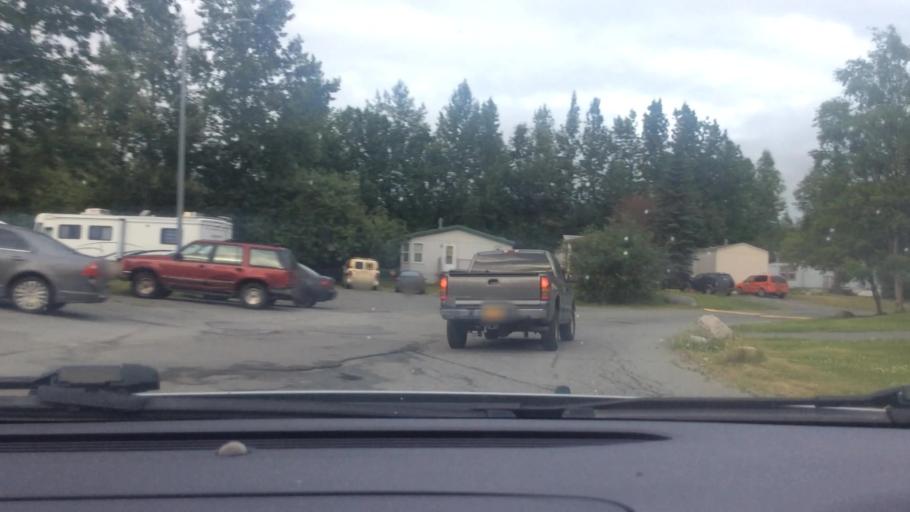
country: US
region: Alaska
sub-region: Anchorage Municipality
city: Elmendorf Air Force Base
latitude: 61.2000
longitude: -149.7278
